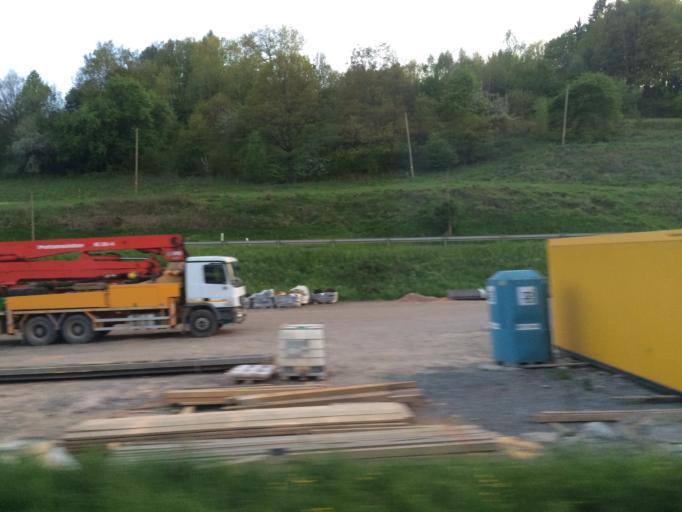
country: DE
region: Bavaria
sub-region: Regierungsbezirk Unterfranken
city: Heigenbrucken
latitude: 50.0253
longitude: 9.3767
